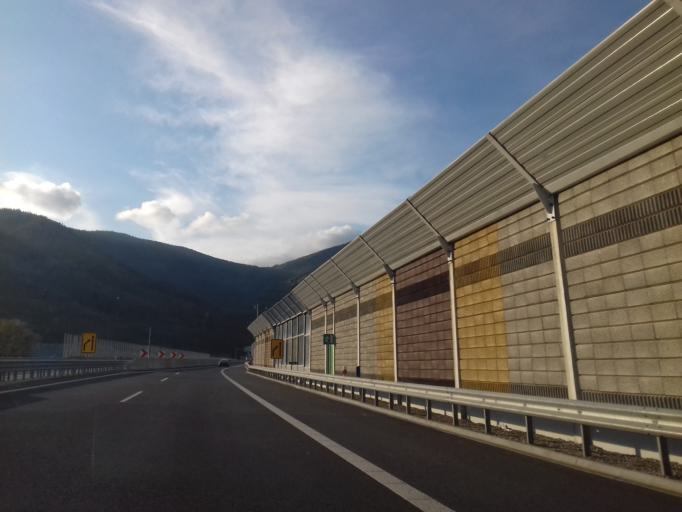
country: SK
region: Zilinsky
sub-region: Okres Zilina
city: Vrutky
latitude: 49.1316
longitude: 18.9040
